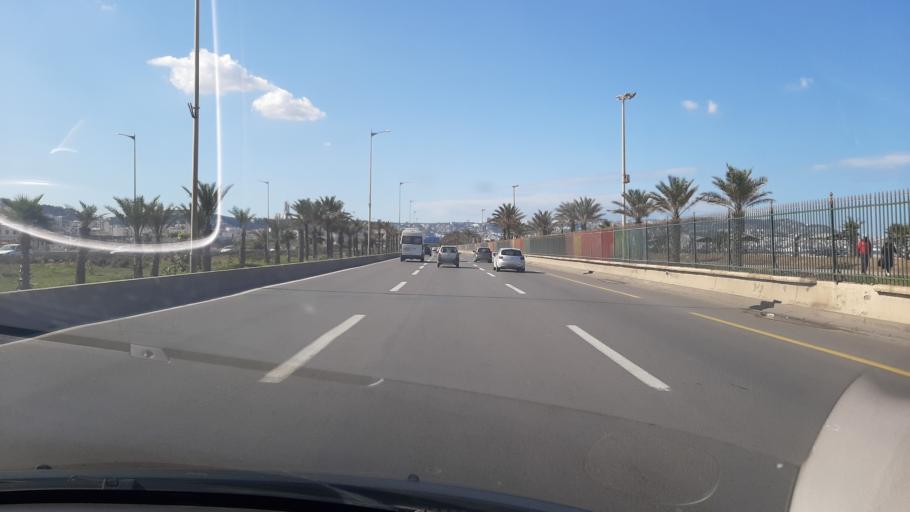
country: DZ
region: Alger
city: Birkhadem
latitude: 36.7444
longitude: 3.1078
